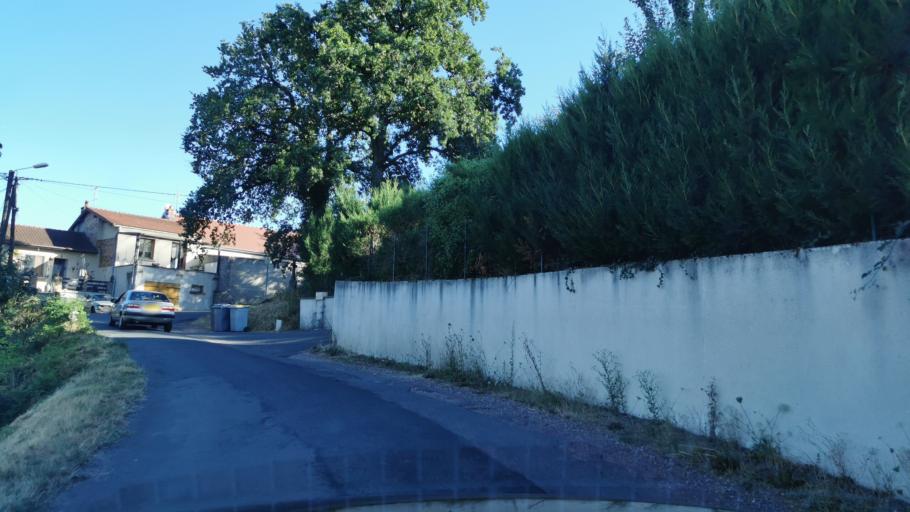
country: FR
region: Bourgogne
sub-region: Departement de Saone-et-Loire
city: Le Creusot
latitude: 46.8084
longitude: 4.3947
